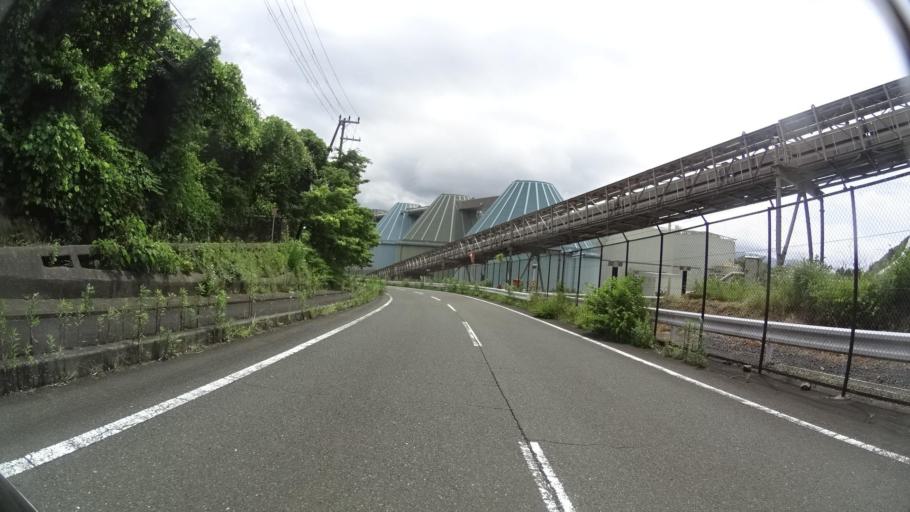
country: JP
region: Kyoto
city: Maizuru
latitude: 35.5290
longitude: 135.3458
